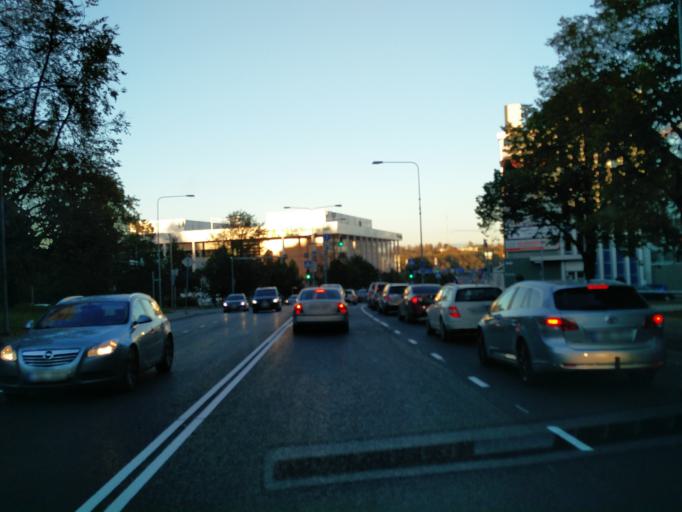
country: EE
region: Tartu
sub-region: Tartu linn
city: Tartu
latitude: 58.3760
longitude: 26.7255
